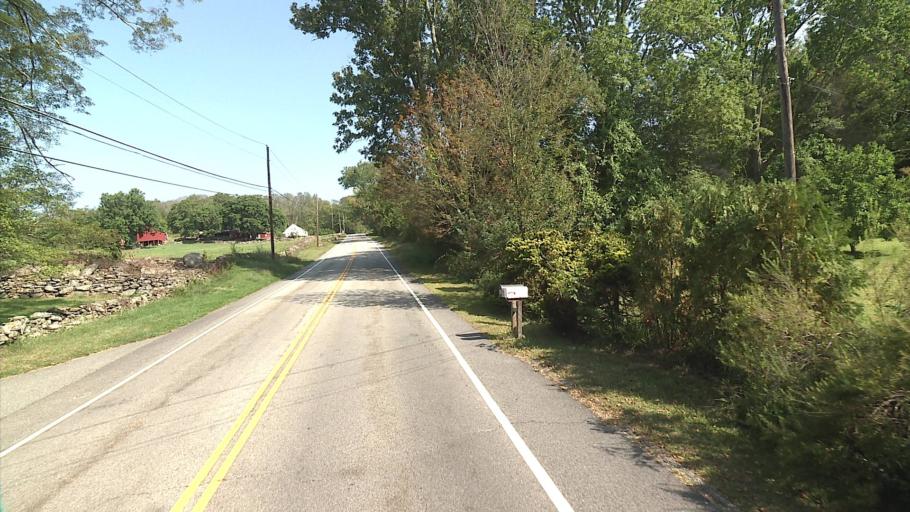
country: US
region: Connecticut
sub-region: Windham County
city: Plainfield Village
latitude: 41.7163
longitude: -71.9710
